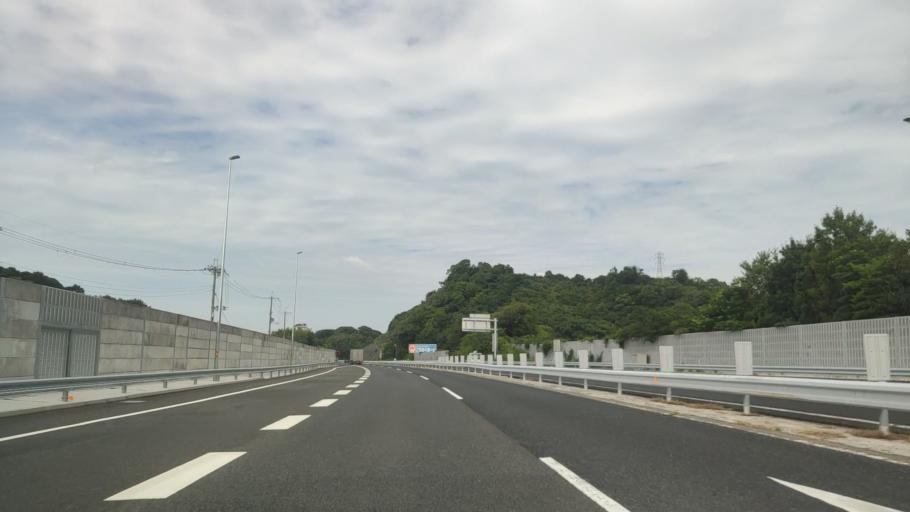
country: JP
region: Wakayama
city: Wakayama-shi
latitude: 34.2100
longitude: 135.2279
